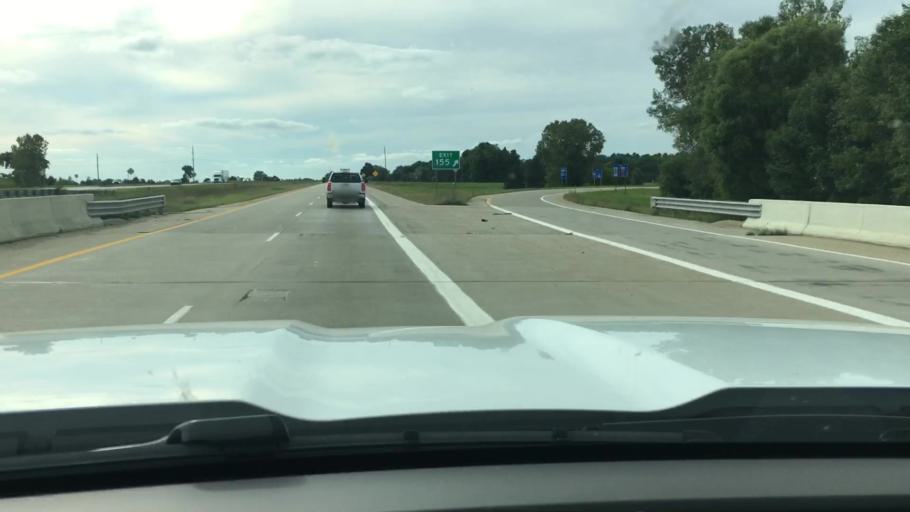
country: US
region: Michigan
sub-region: Lapeer County
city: Lapeer
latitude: 43.0248
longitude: -83.3136
